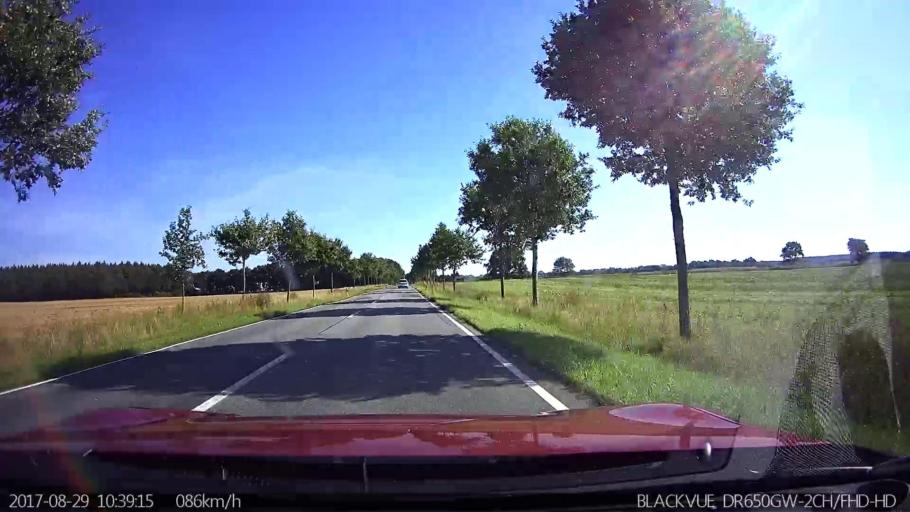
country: DE
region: Mecklenburg-Vorpommern
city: Franzburg
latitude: 54.1733
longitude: 12.8308
